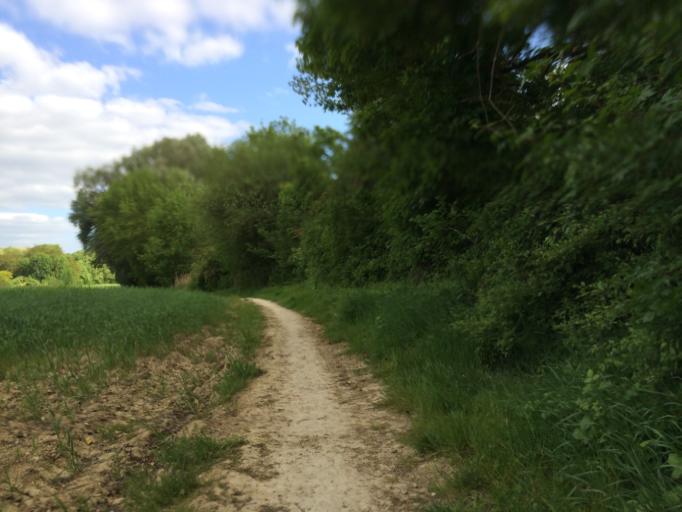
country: FR
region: Ile-de-France
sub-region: Departement de l'Essonne
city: Viry-Chatillon
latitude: 48.6719
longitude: 2.3999
